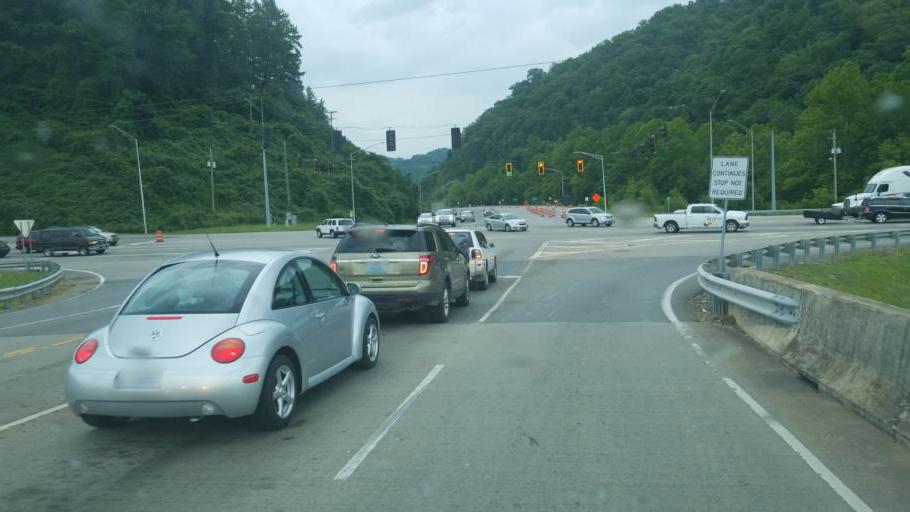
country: US
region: Kentucky
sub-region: Pike County
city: Coal Run Village
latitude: 37.5036
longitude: -82.5330
